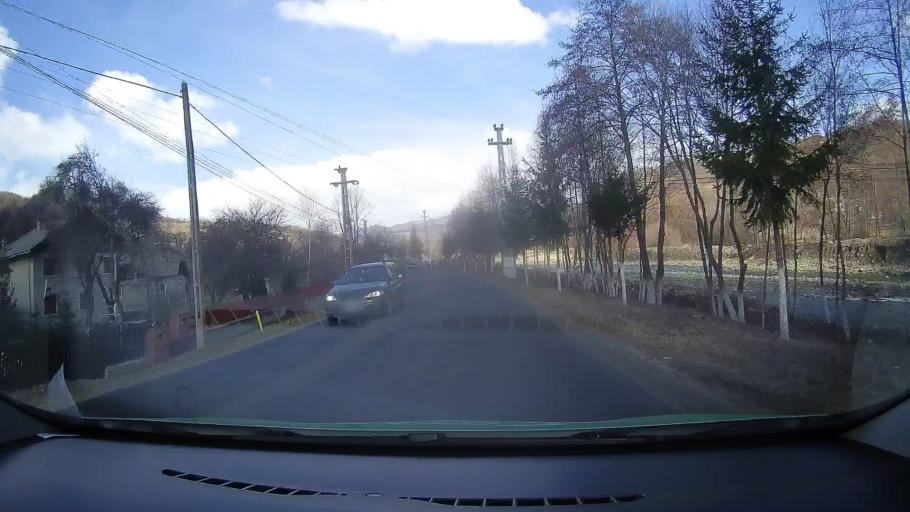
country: RO
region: Dambovita
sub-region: Comuna Runcu
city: Badeni
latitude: 45.1598
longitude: 25.3972
